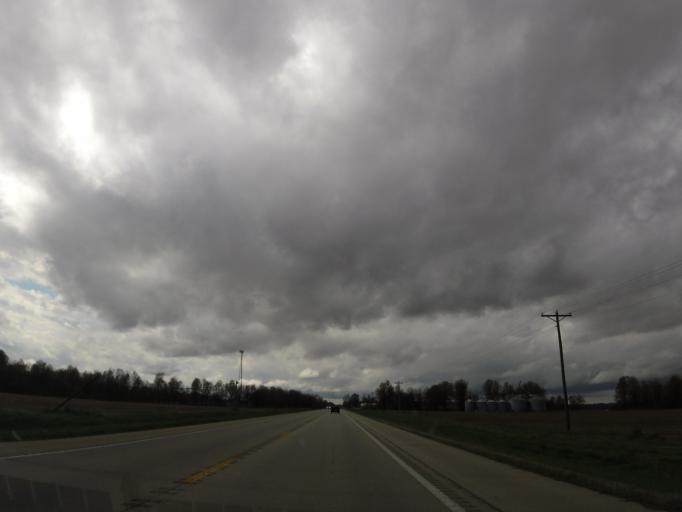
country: US
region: Arkansas
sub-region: Clay County
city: Corning
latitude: 36.5758
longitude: -90.5208
